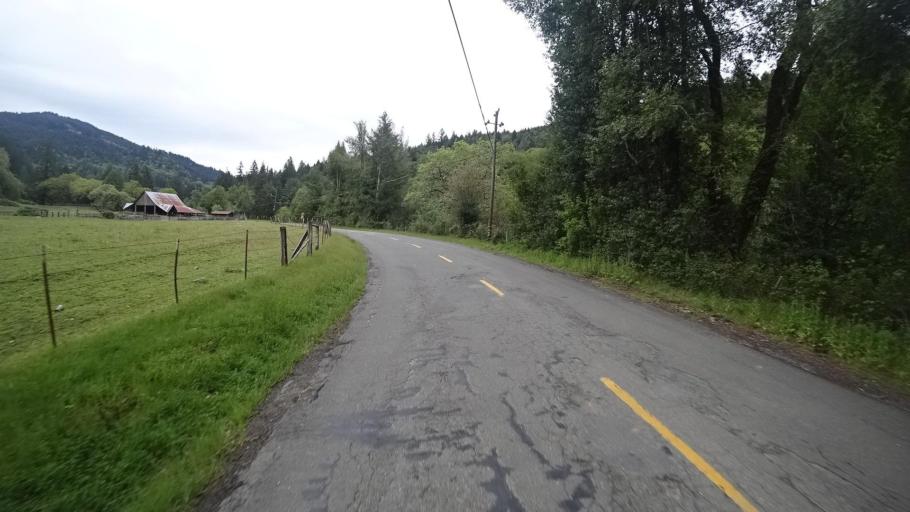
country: US
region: California
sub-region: Humboldt County
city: Blue Lake
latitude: 40.9661
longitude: -123.8423
